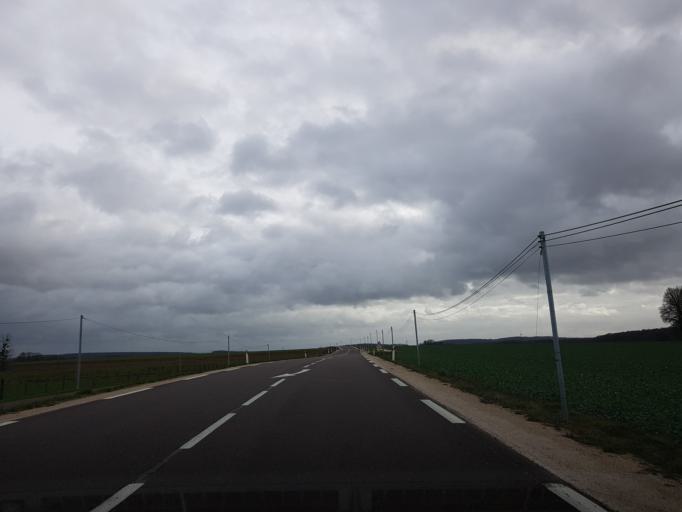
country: FR
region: Champagne-Ardenne
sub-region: Departement de la Haute-Marne
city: Fayl-Billot
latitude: 47.7665
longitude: 5.7089
